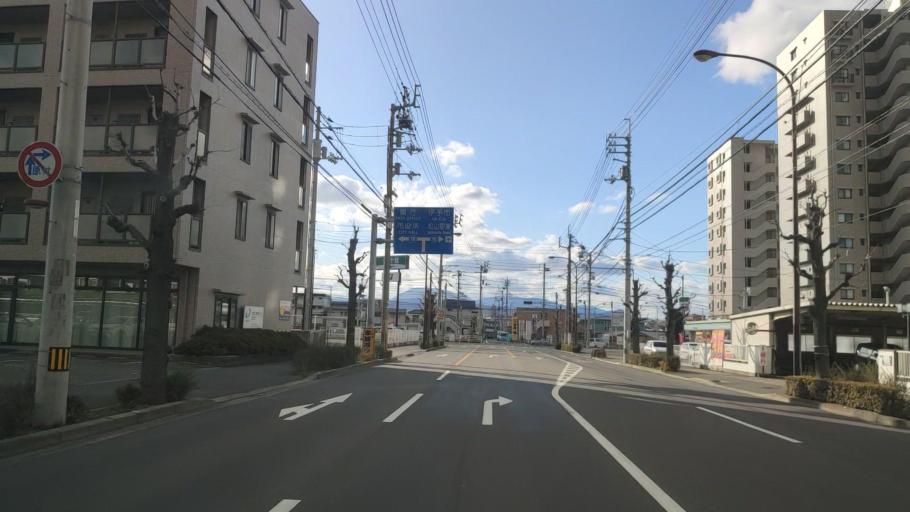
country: JP
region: Ehime
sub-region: Shikoku-chuo Shi
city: Matsuyama
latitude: 33.8312
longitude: 132.7525
